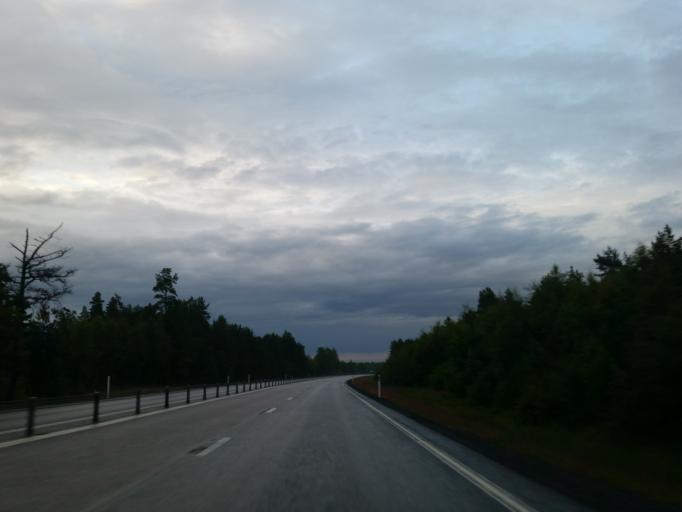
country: SE
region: Vaesterbotten
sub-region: Umea Kommun
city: Saevar
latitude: 63.9498
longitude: 20.6629
